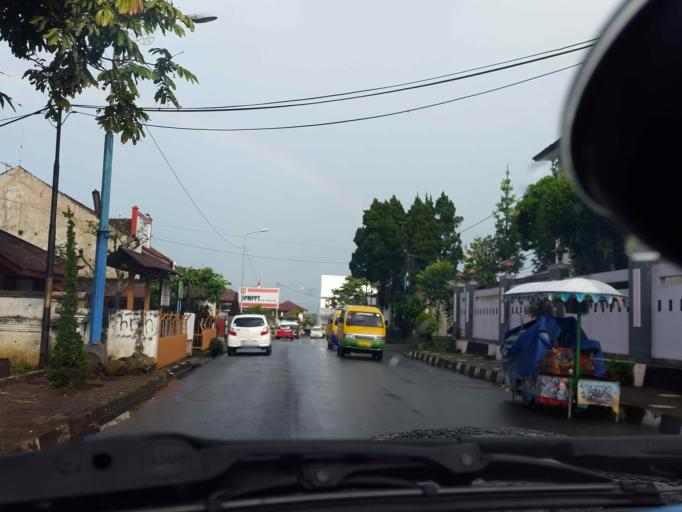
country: ID
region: Central Java
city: Wonosobo
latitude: -7.3588
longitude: 109.9014
